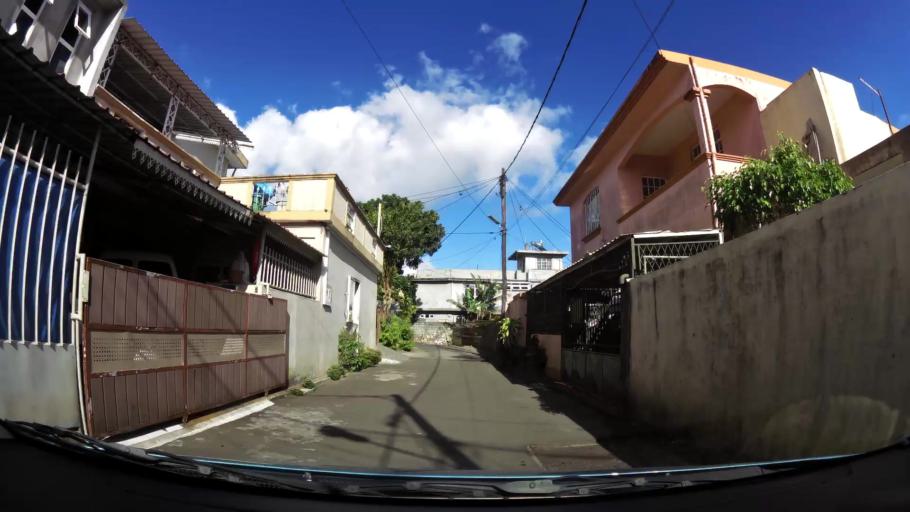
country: MU
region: Plaines Wilhems
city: Curepipe
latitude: -20.3013
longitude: 57.5187
